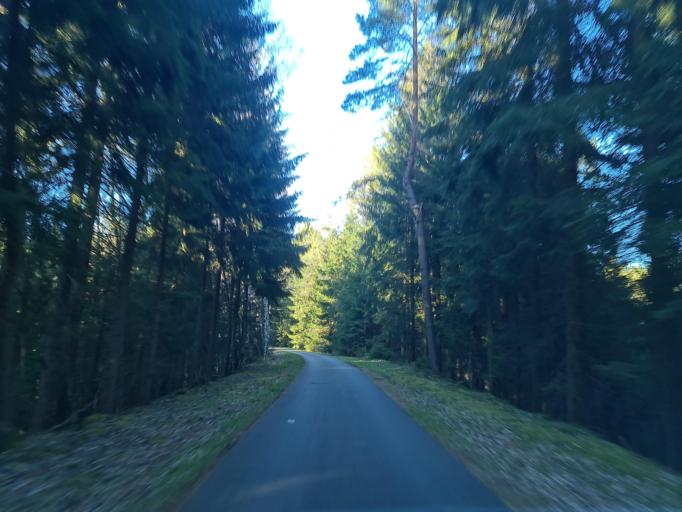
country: DE
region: Saxony
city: Neustadt Vogtland
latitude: 50.4716
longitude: 12.3098
